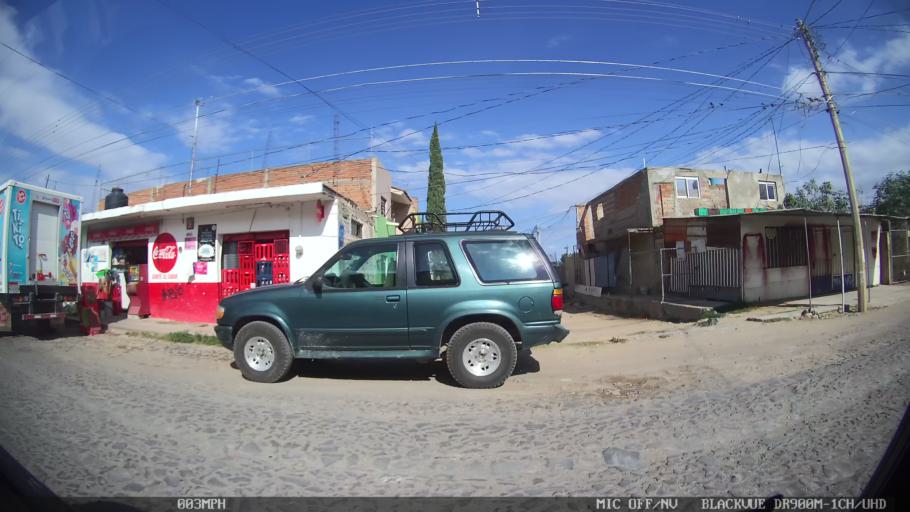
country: MX
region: Jalisco
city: Tonala
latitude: 20.6507
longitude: -103.2517
